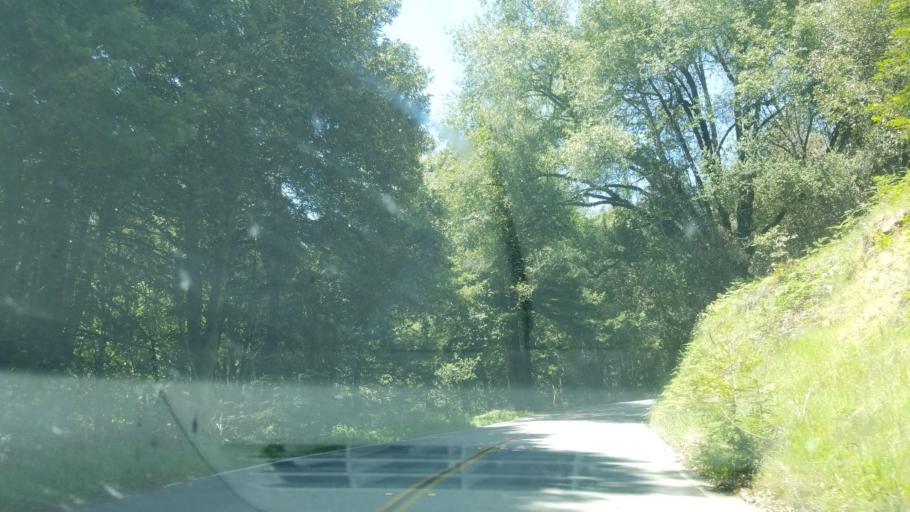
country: US
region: California
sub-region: Santa Cruz County
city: Interlaken
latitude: 37.0062
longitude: -121.7124
